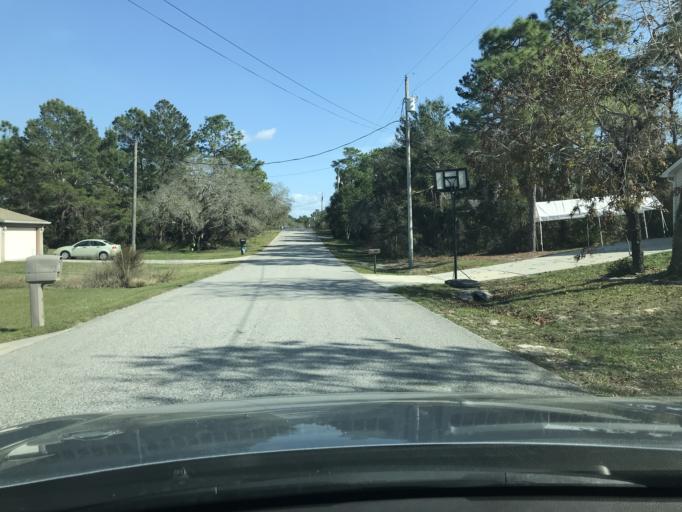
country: US
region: Florida
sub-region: Hernando County
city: North Weeki Wachee
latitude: 28.5415
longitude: -82.5508
